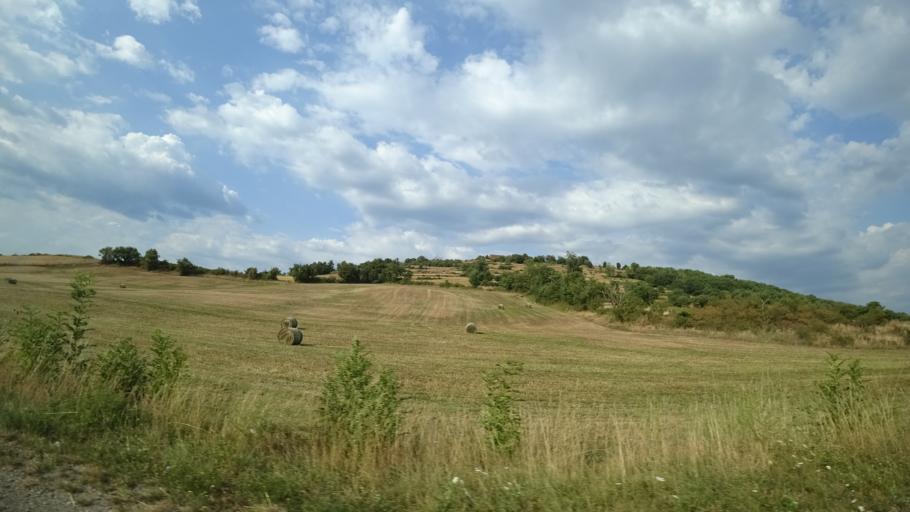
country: FR
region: Midi-Pyrenees
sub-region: Departement de l'Aveyron
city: Saint-Christophe-Vallon
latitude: 44.4877
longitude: 2.3937
